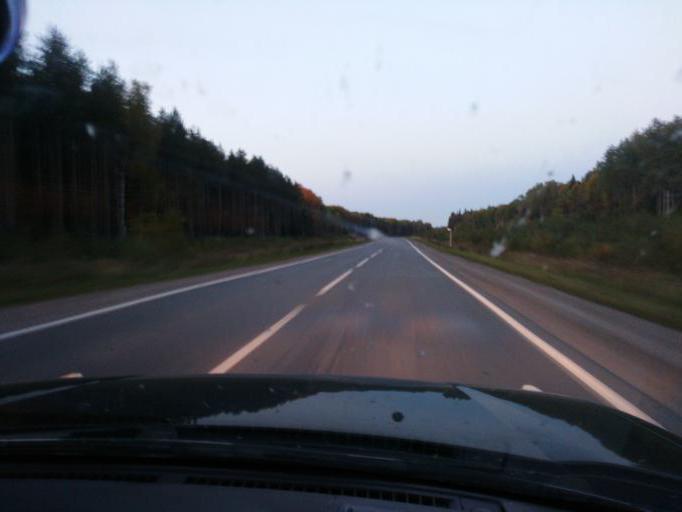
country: RU
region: Perm
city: Verkhnechusovskiye Gorodki
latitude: 58.2388
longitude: 57.2236
